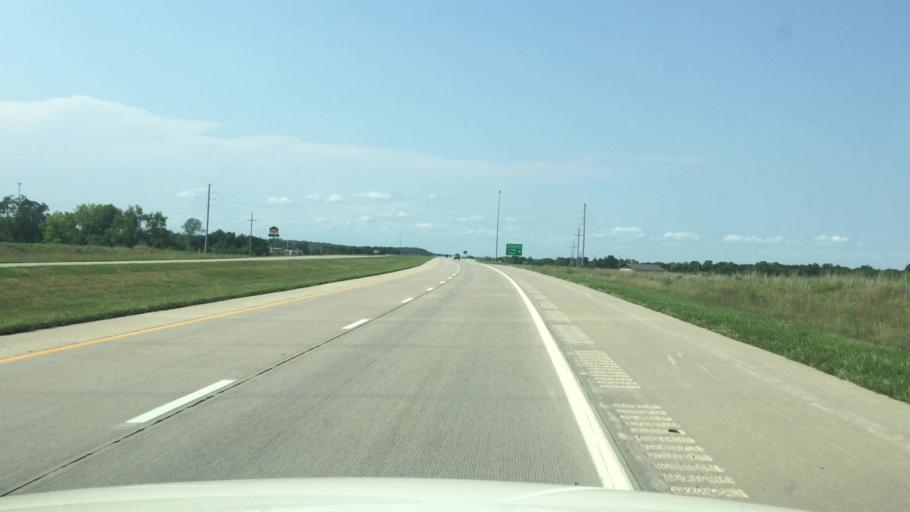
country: US
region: Kansas
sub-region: Linn County
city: Pleasanton
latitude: 38.1761
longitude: -94.6967
